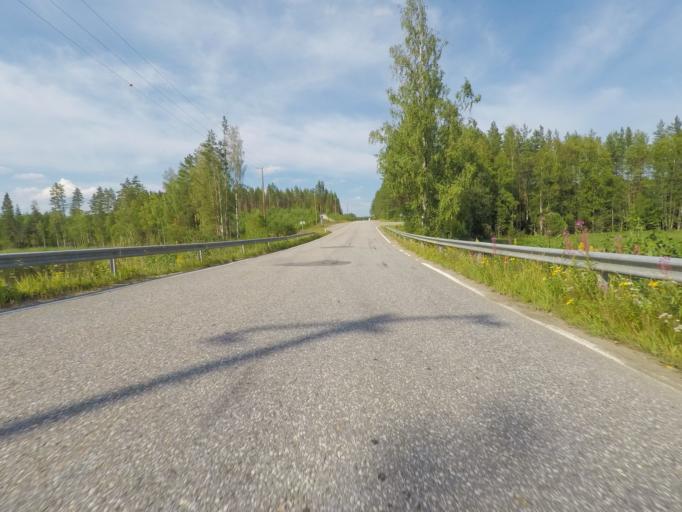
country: FI
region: Southern Savonia
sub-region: Savonlinna
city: Sulkava
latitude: 61.7824
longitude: 28.2397
